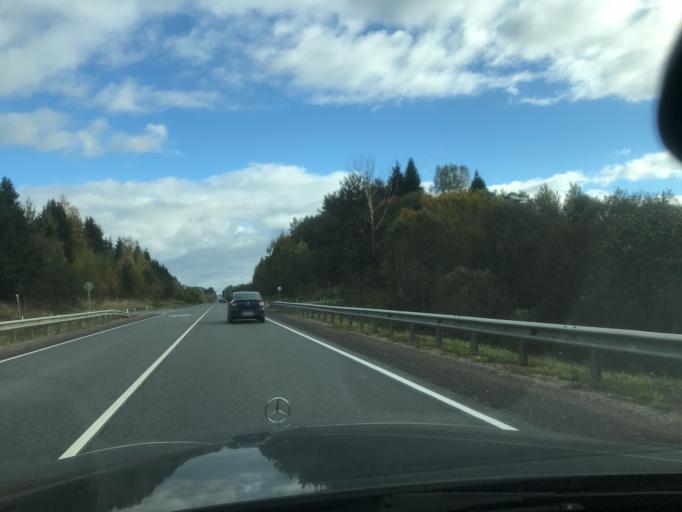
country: RU
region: Pskov
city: Opochka
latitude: 56.6551
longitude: 28.7582
